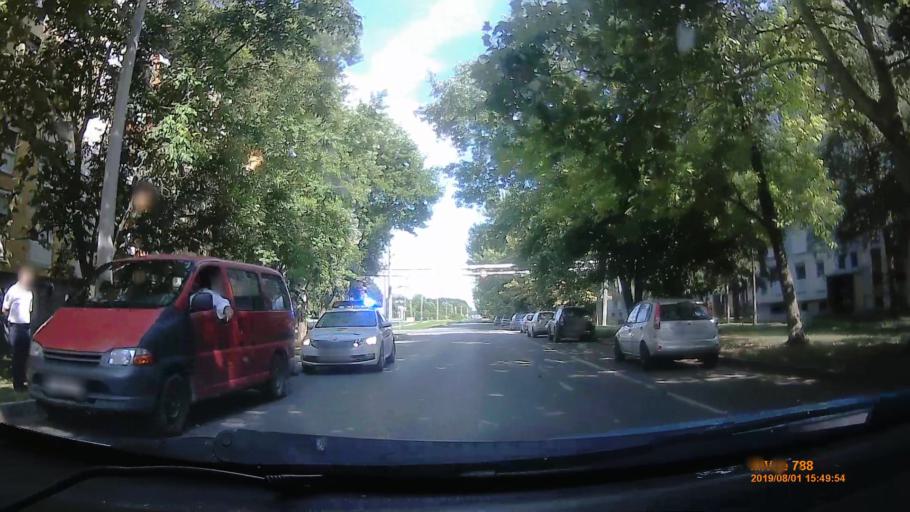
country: HU
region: Baranya
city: Szentlorinc
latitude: 46.0384
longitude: 17.9942
